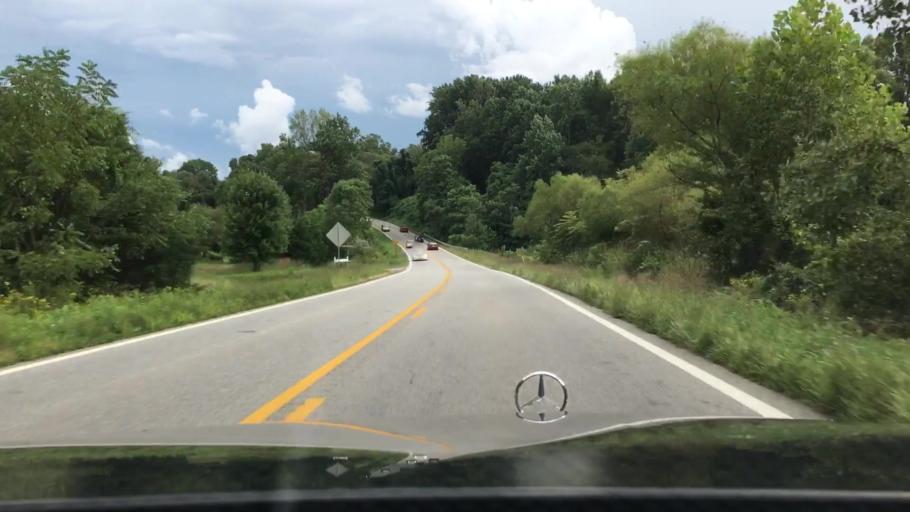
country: US
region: Virginia
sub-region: Nelson County
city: Nellysford
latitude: 37.9800
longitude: -78.8394
